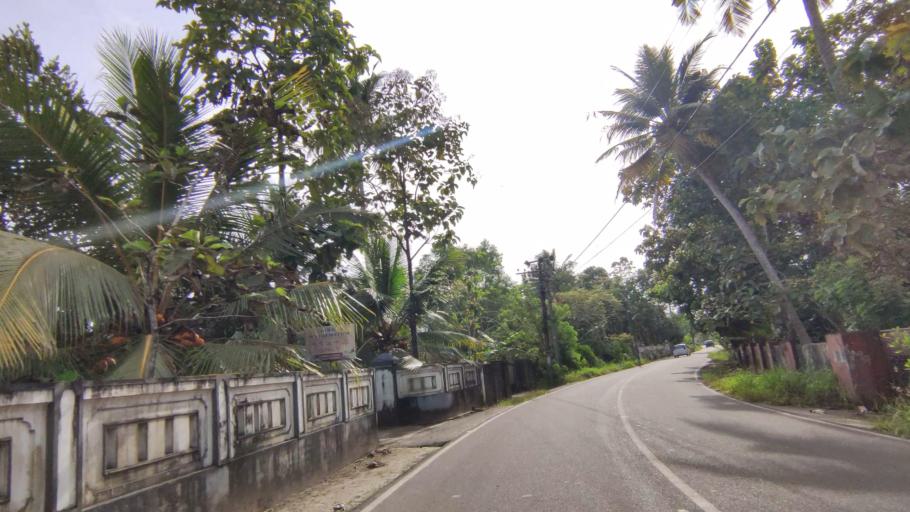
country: IN
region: Kerala
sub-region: Alappuzha
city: Shertallai
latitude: 9.6374
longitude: 76.3367
